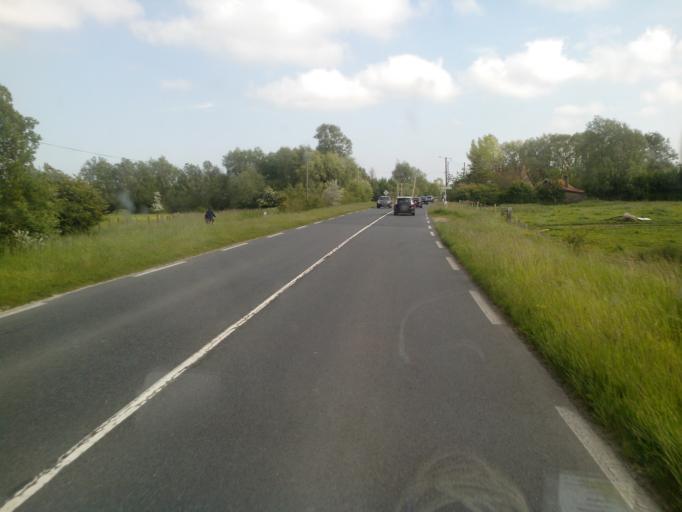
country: FR
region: Picardie
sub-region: Departement de la Somme
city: Saint-Valery-sur-Somme
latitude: 50.1942
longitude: 1.6981
